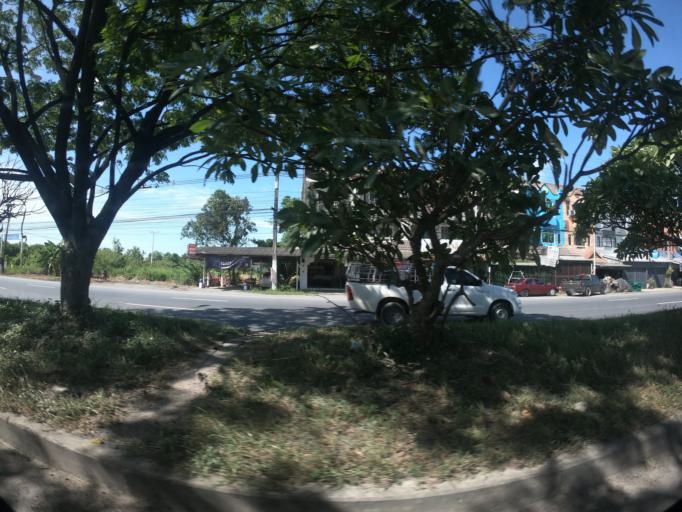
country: TH
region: Nakhon Nayok
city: Ban Na
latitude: 14.2550
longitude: 101.0873
